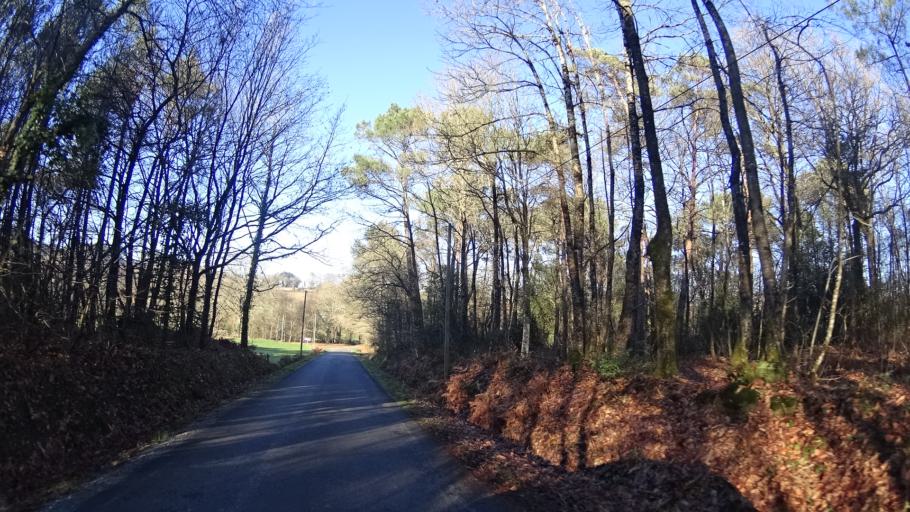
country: FR
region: Brittany
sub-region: Departement du Morbihan
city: Allaire
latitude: 47.6178
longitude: -2.1929
